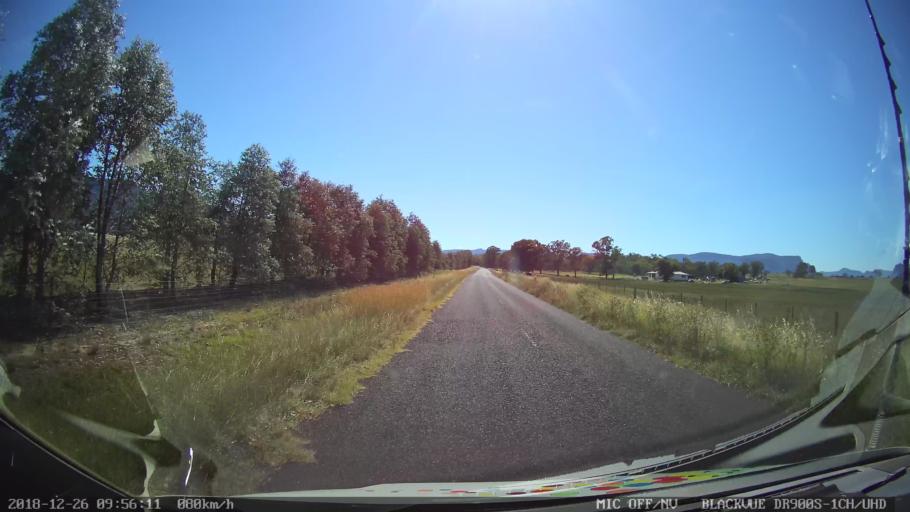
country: AU
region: New South Wales
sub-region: Mid-Western Regional
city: Kandos
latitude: -33.0405
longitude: 150.1757
